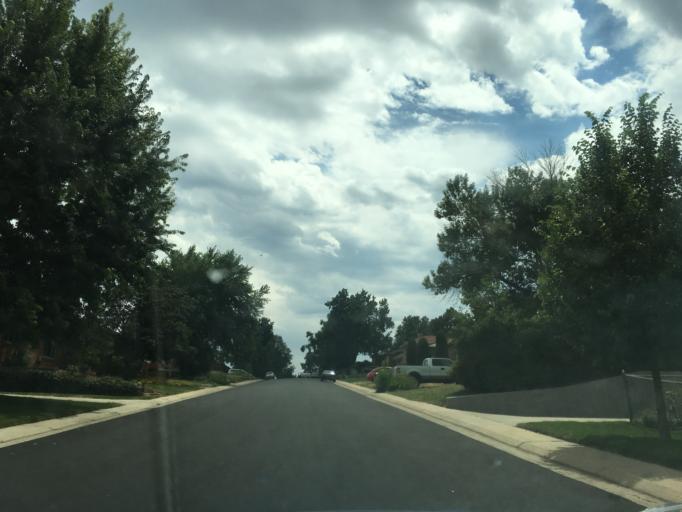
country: US
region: Colorado
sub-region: Arapahoe County
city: Sheridan
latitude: 39.6765
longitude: -105.0480
